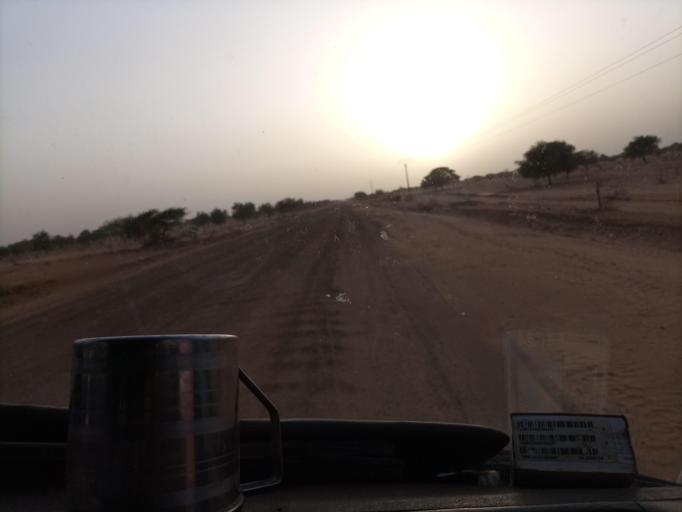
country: SN
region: Louga
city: Dara
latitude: 15.4080
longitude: -15.6765
